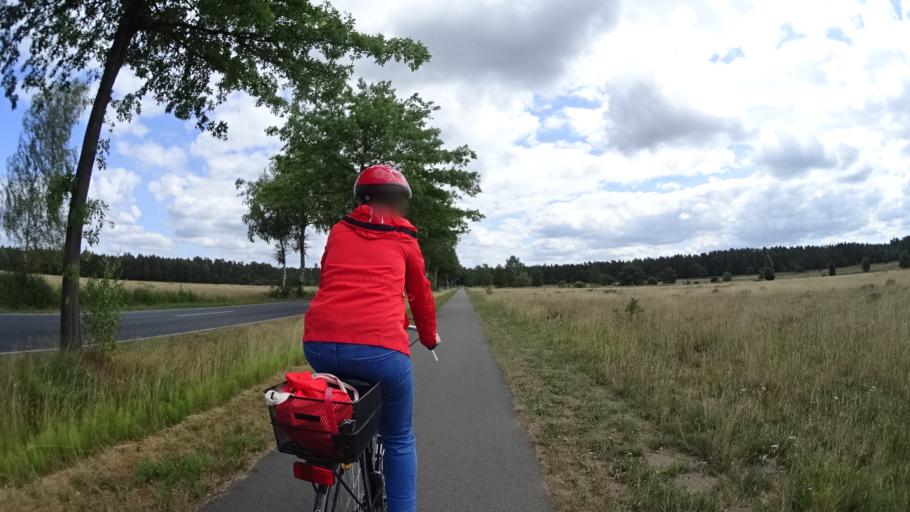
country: DE
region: Lower Saxony
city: Handeloh
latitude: 53.2377
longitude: 9.8768
